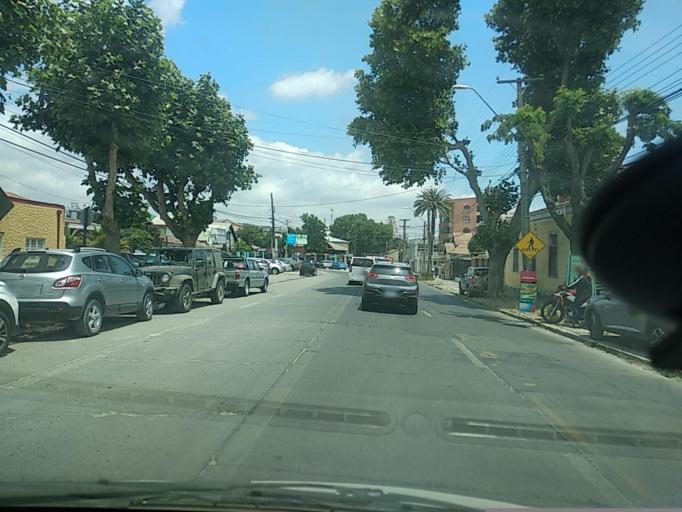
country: CL
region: Valparaiso
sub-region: Provincia de Marga Marga
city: Quilpue
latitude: -33.0446
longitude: -71.4372
